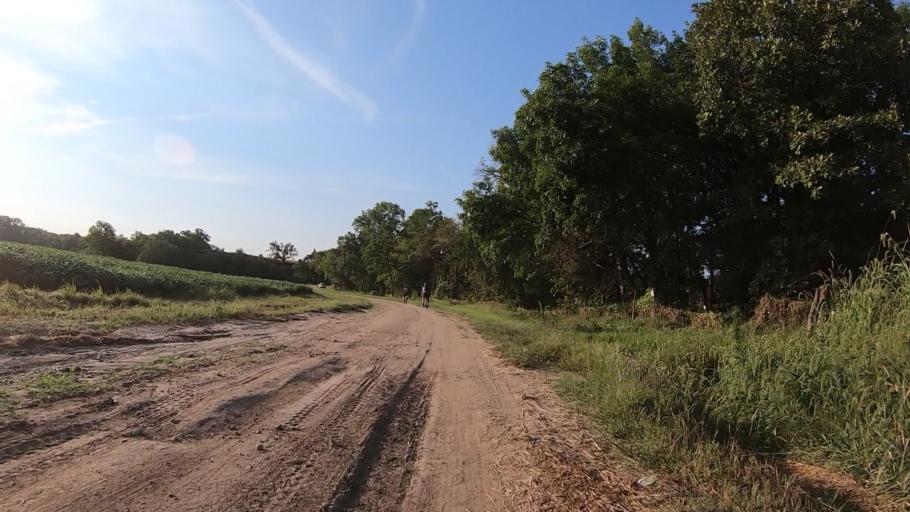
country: US
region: Kansas
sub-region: Marshall County
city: Blue Rapids
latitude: 39.7220
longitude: -96.8067
